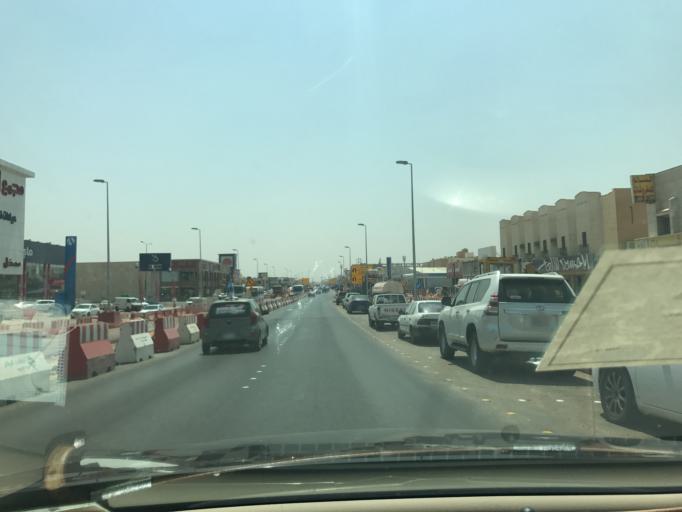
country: SA
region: Ar Riyad
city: Riyadh
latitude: 24.7511
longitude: 46.7715
